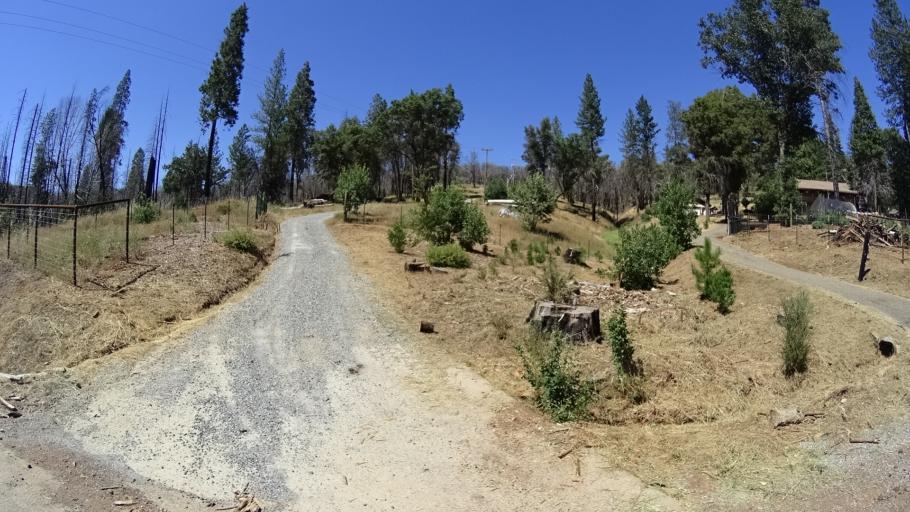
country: US
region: California
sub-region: Calaveras County
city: Mountain Ranch
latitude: 38.2832
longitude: -120.5567
